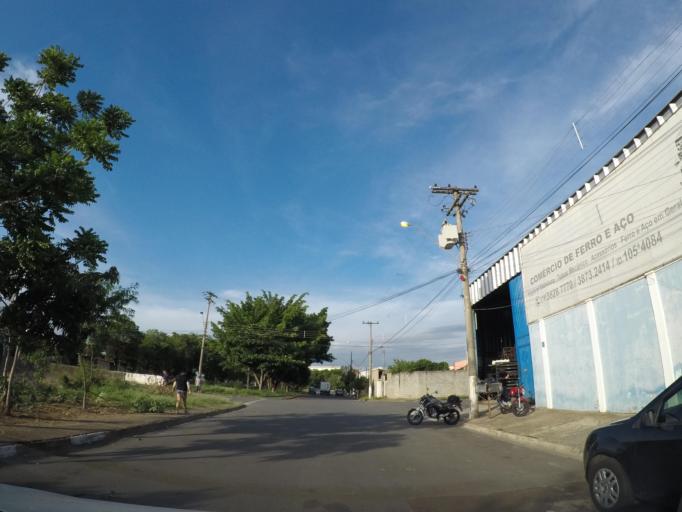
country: BR
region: Sao Paulo
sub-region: Sumare
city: Sumare
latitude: -22.8141
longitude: -47.2637
